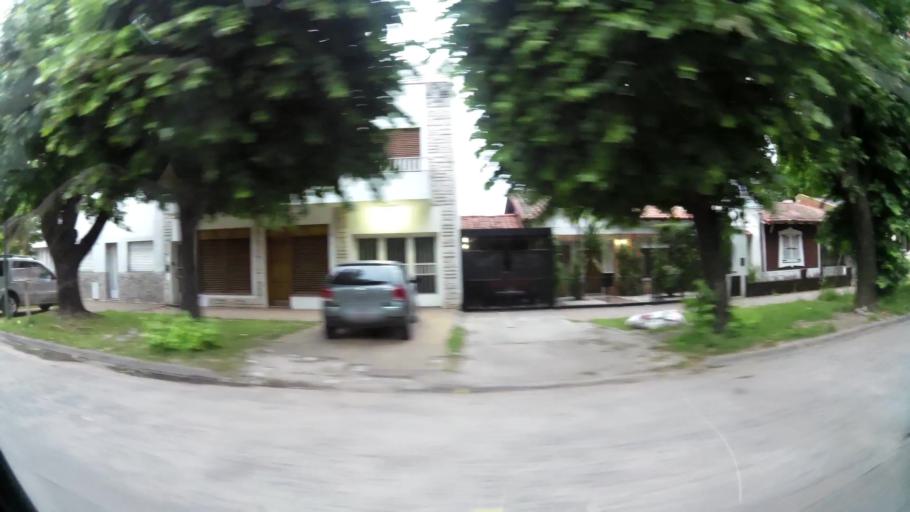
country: AR
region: Buenos Aires
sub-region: Partido de La Plata
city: La Plata
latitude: -34.9105
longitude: -57.9799
